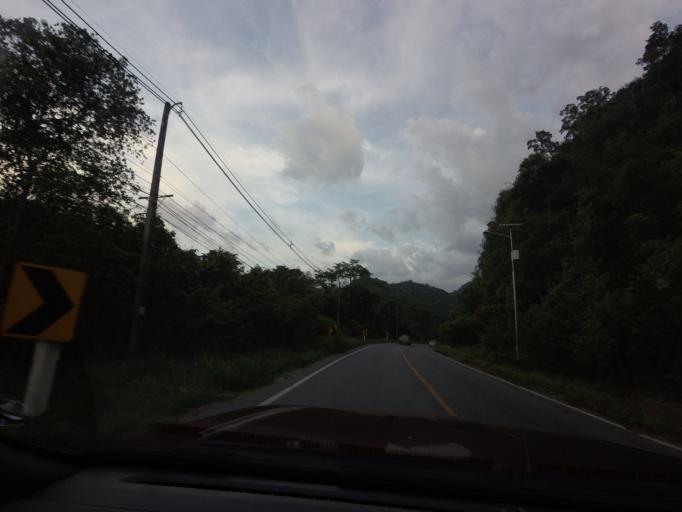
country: TH
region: Yala
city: Than To
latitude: 6.0174
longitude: 101.2009
